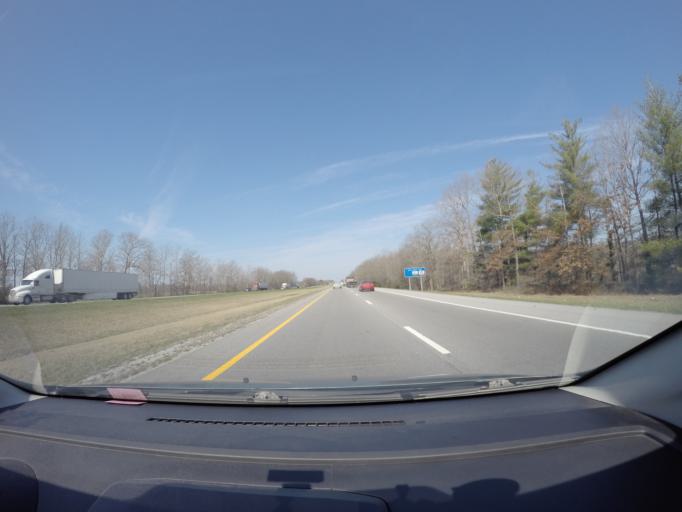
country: US
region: Tennessee
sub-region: Coffee County
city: New Union
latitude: 35.5273
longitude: -86.1430
